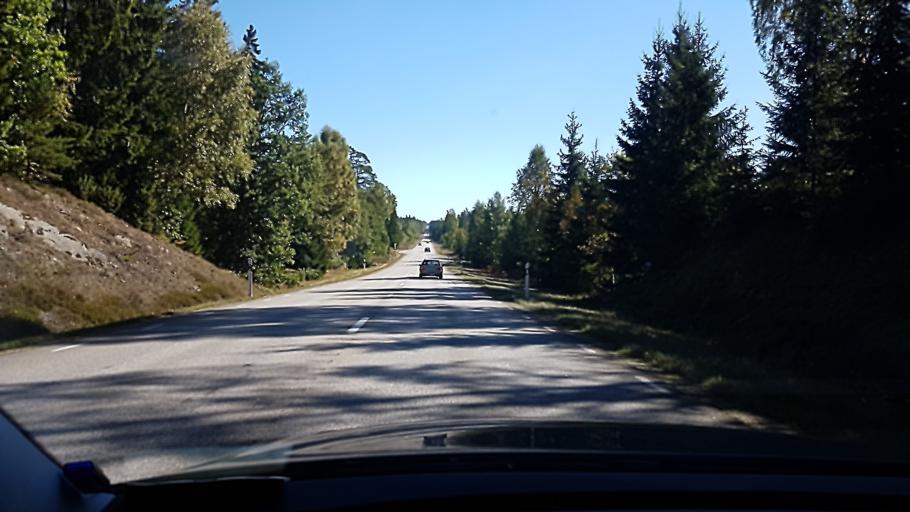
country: SE
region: Kronoberg
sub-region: Lessebo Kommun
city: Lessebo
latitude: 56.7298
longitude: 15.3636
